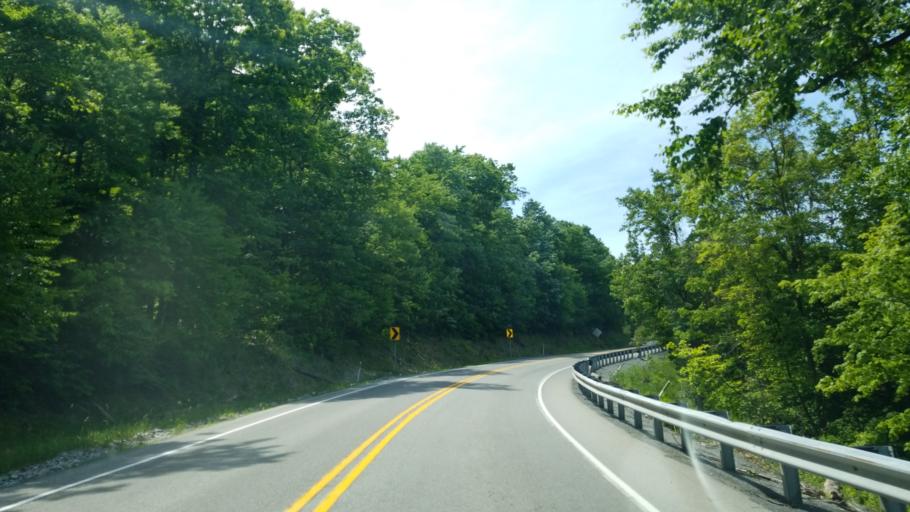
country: US
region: Pennsylvania
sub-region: Blair County
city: Tyrone
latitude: 40.7038
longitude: -78.2923
